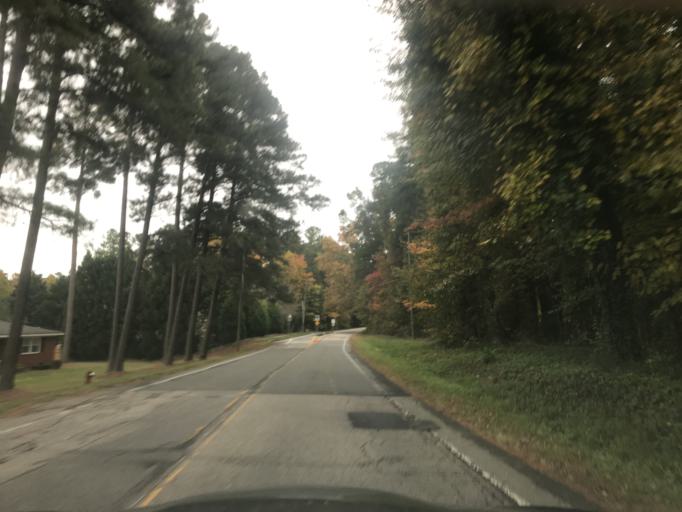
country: US
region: North Carolina
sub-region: Wake County
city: West Raleigh
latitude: 35.8558
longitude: -78.6767
